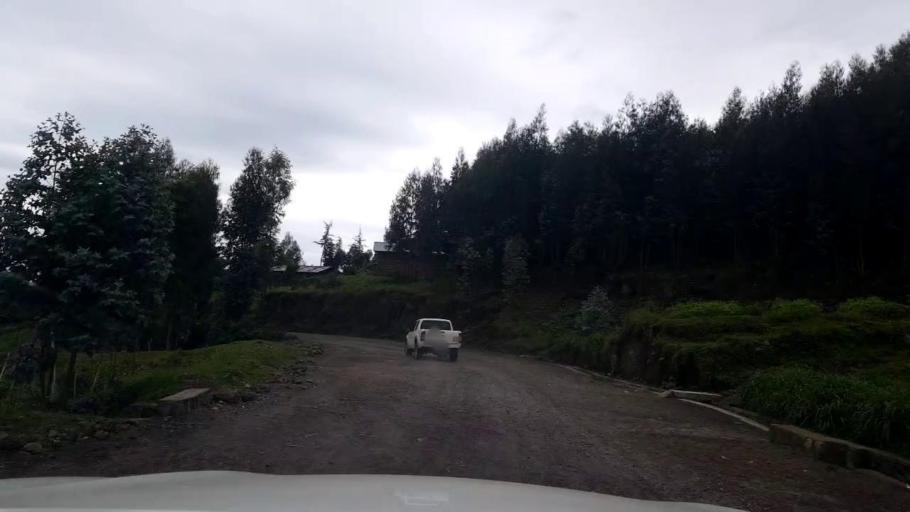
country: RW
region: Northern Province
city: Musanze
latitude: -1.5085
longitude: 29.5329
